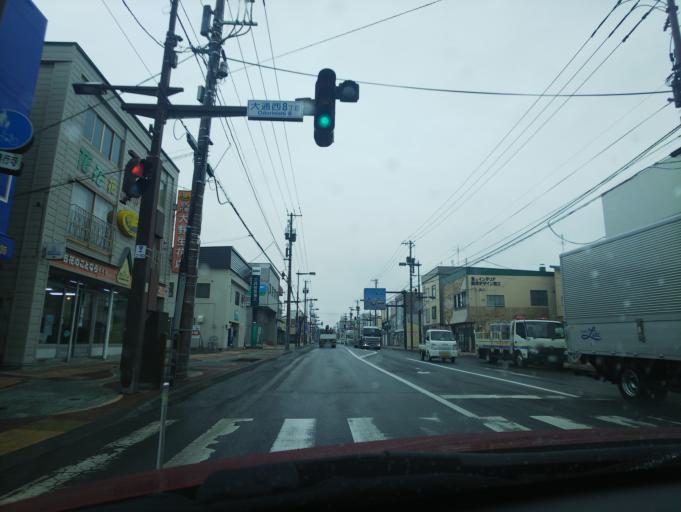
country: JP
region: Hokkaido
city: Nayoro
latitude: 44.1731
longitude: 142.3931
